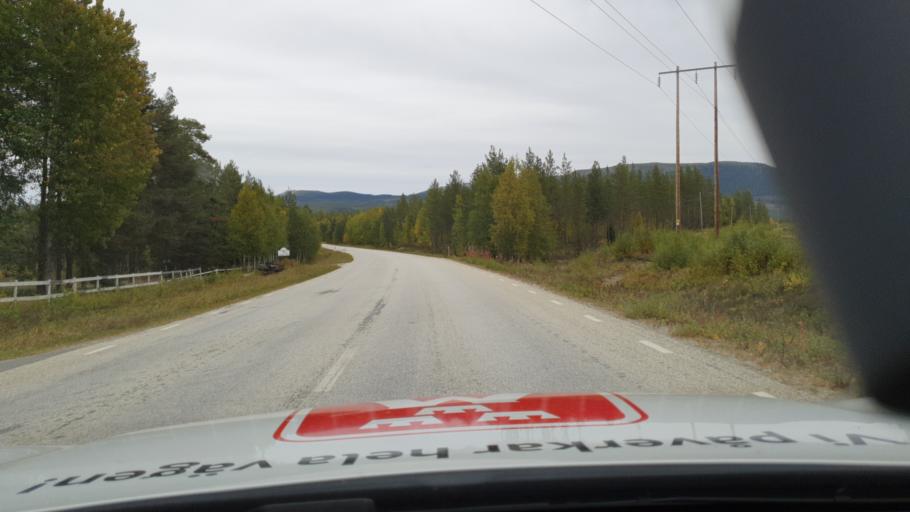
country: SE
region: Jaemtland
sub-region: Harjedalens Kommun
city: Sveg
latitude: 62.4276
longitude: 13.8265
